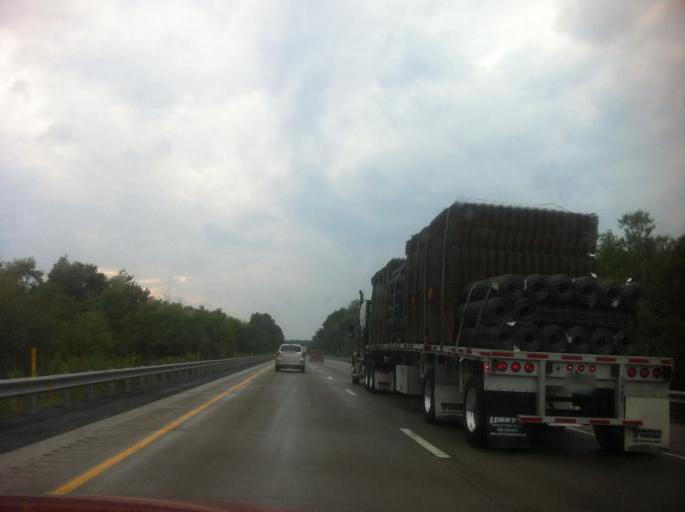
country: US
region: Pennsylvania
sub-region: Jefferson County
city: Falls Creek
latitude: 41.1539
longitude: -78.8091
